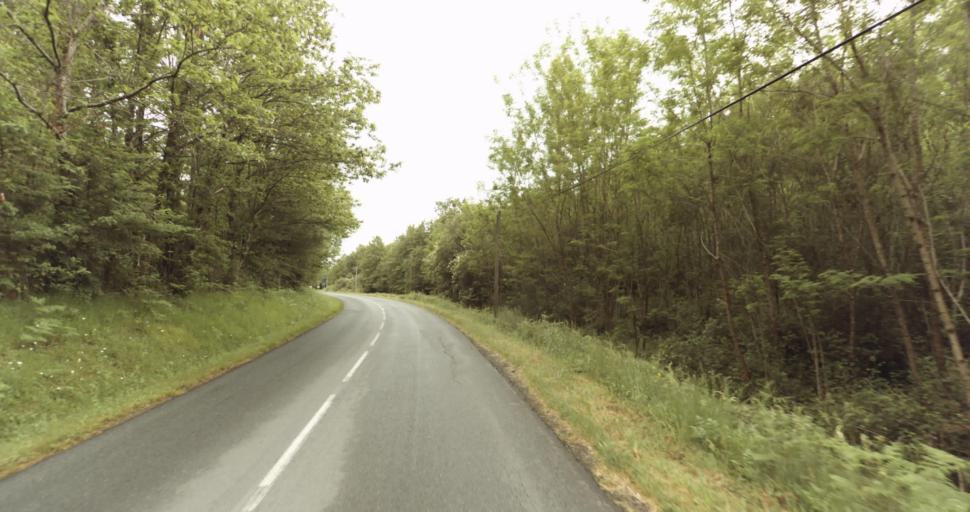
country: FR
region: Aquitaine
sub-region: Departement de la Dordogne
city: Belves
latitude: 44.7118
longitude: 0.9339
